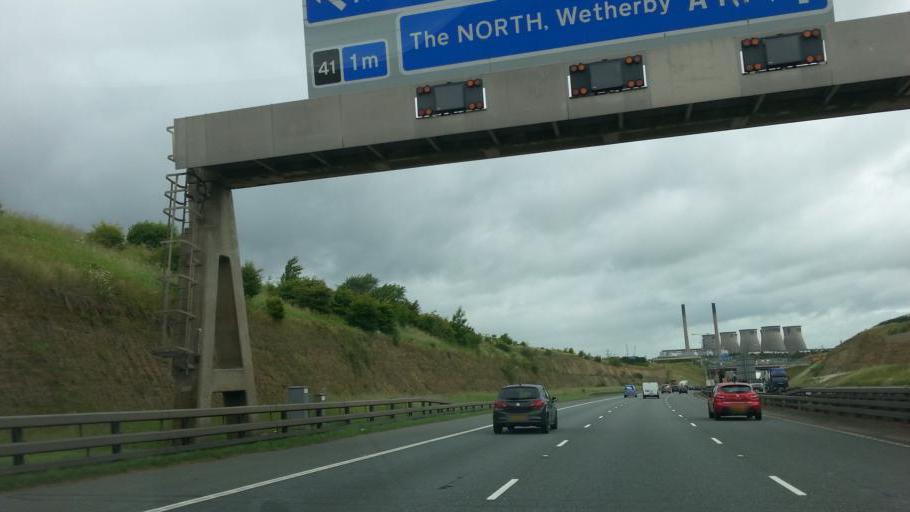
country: GB
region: England
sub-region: City and Borough of Wakefield
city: Ferrybridge
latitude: 53.6940
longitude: -1.2748
